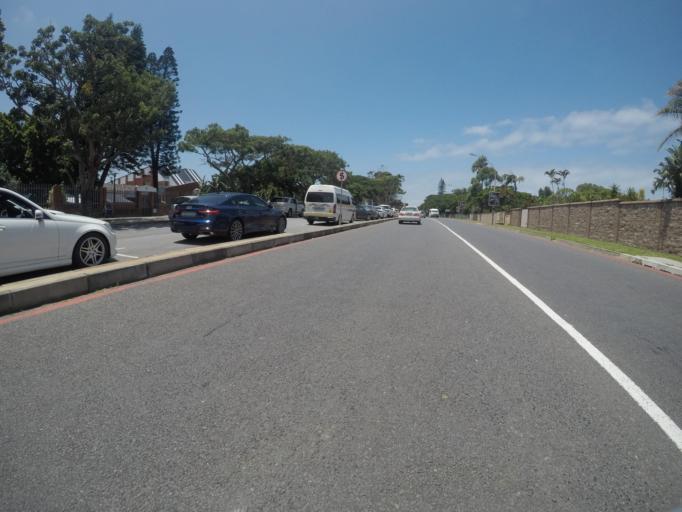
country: ZA
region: Eastern Cape
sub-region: Buffalo City Metropolitan Municipality
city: East London
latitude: -32.9950
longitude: 27.9247
